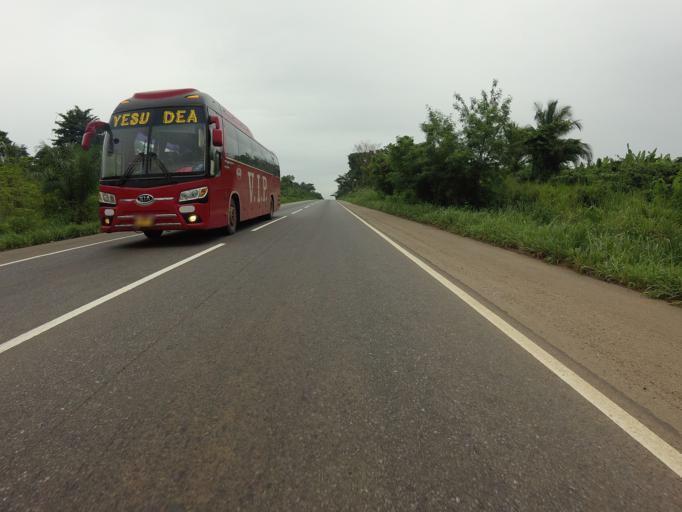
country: GH
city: Kibi
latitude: 6.1852
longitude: -0.4705
